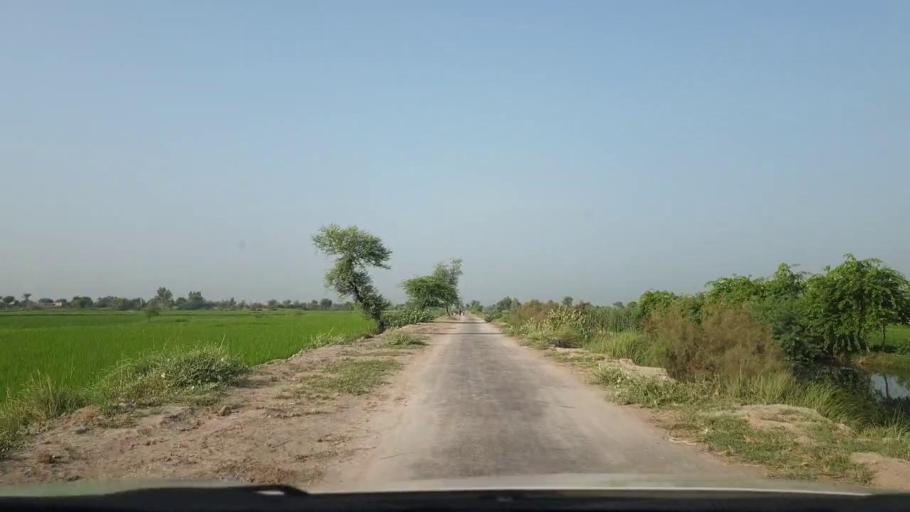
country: PK
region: Sindh
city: Larkana
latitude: 27.4977
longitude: 68.1726
